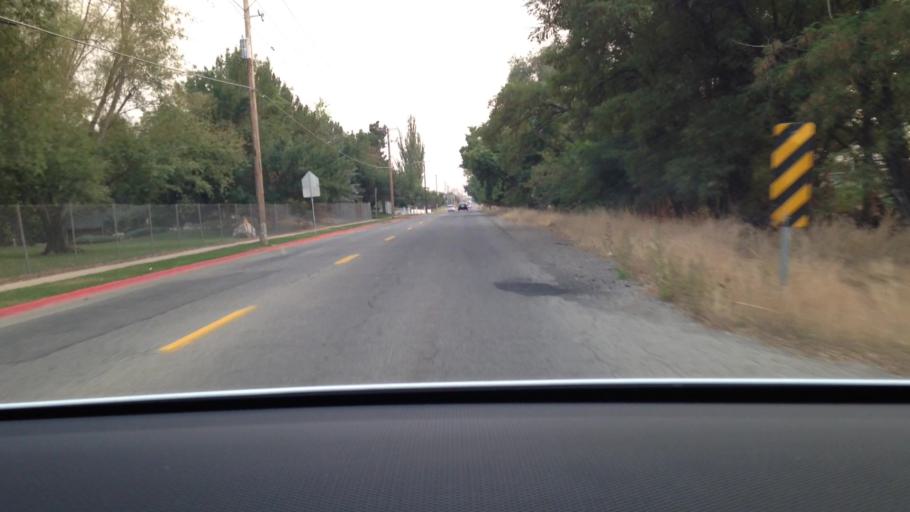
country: US
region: Utah
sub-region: Davis County
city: Layton
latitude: 41.0737
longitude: -112.0070
